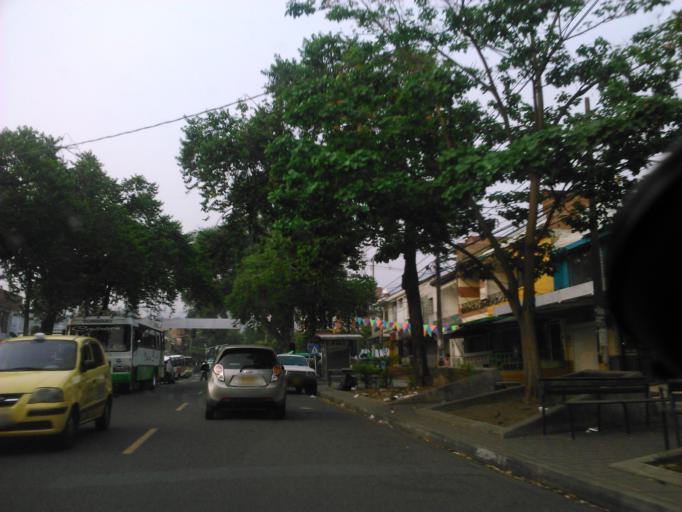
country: CO
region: Antioquia
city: Medellin
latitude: 6.2582
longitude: -75.6141
